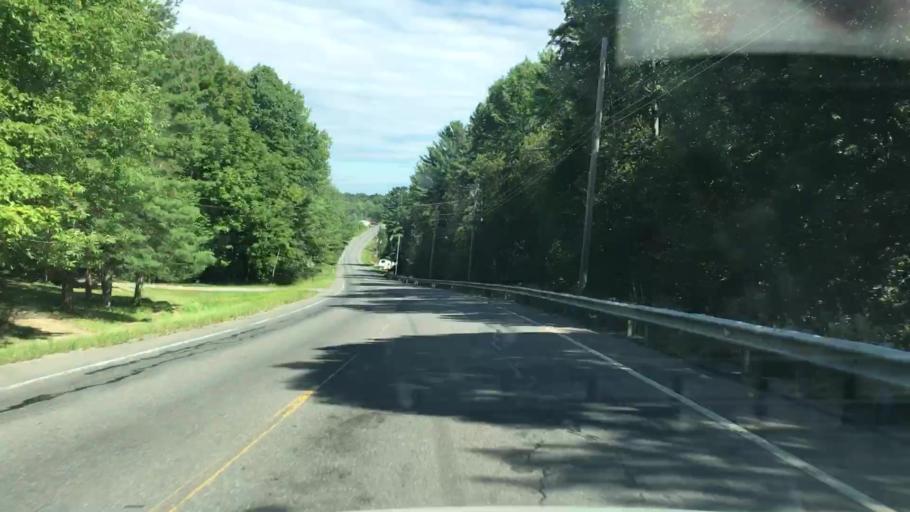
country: US
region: Maine
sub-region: Penobscot County
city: Dexter
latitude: 45.0765
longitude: -69.2316
